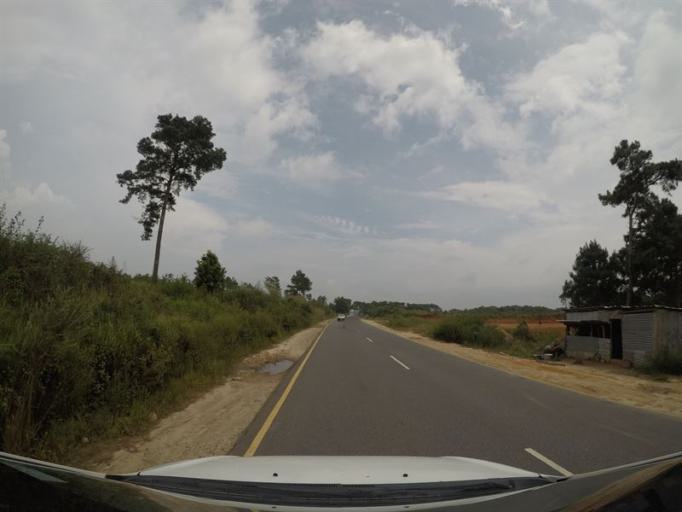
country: IN
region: Meghalaya
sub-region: East Khasi Hills
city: Shillong
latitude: 25.4906
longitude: 92.1872
